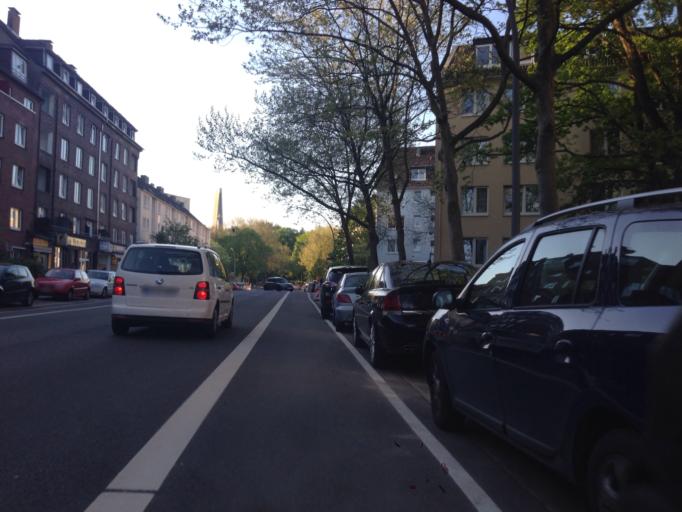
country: DE
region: Hamburg
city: Borgfelde
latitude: 53.5526
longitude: 10.0582
